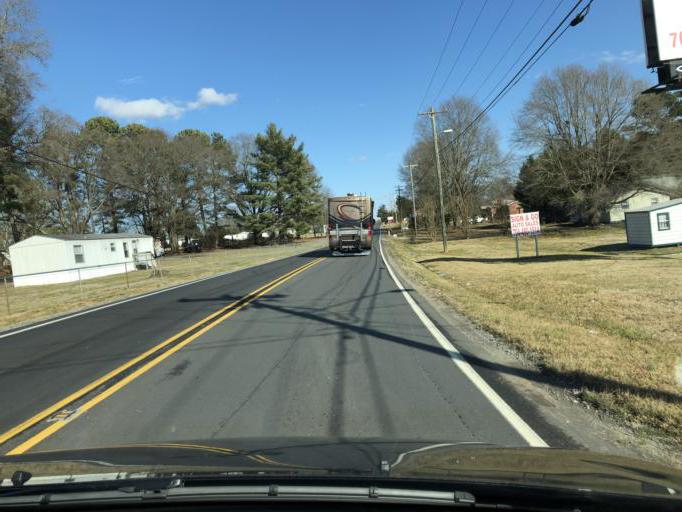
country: US
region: North Carolina
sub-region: Cleveland County
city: Shelby
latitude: 35.2252
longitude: -81.5280
